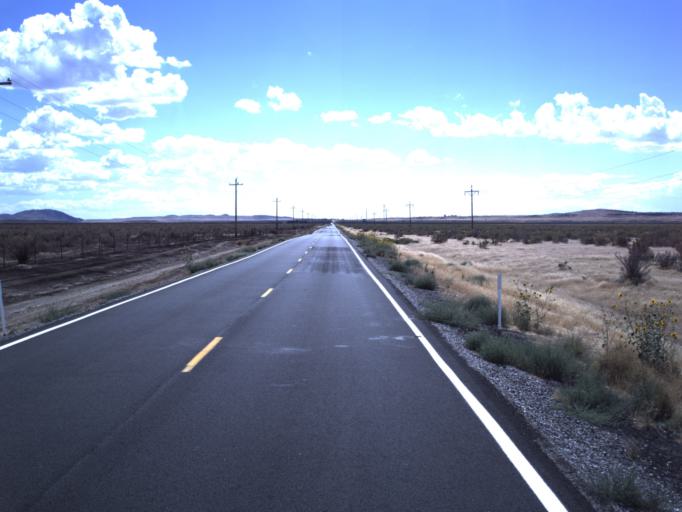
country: US
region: Utah
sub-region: Tooele County
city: Grantsville
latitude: 40.2731
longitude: -112.6787
